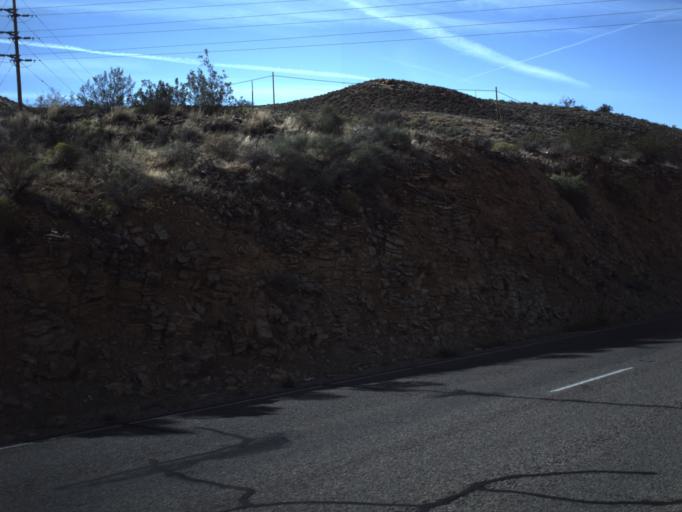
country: US
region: Utah
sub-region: Washington County
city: LaVerkin
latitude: 37.2187
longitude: -113.2617
